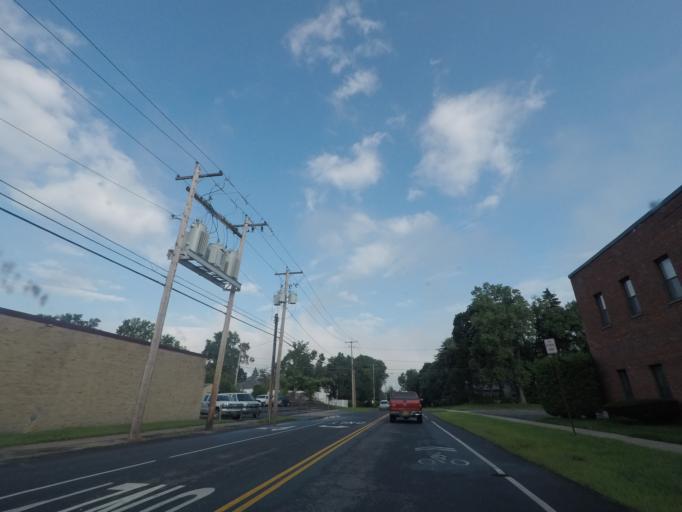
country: US
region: New York
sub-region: Albany County
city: West Albany
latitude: 42.6783
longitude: -73.7962
